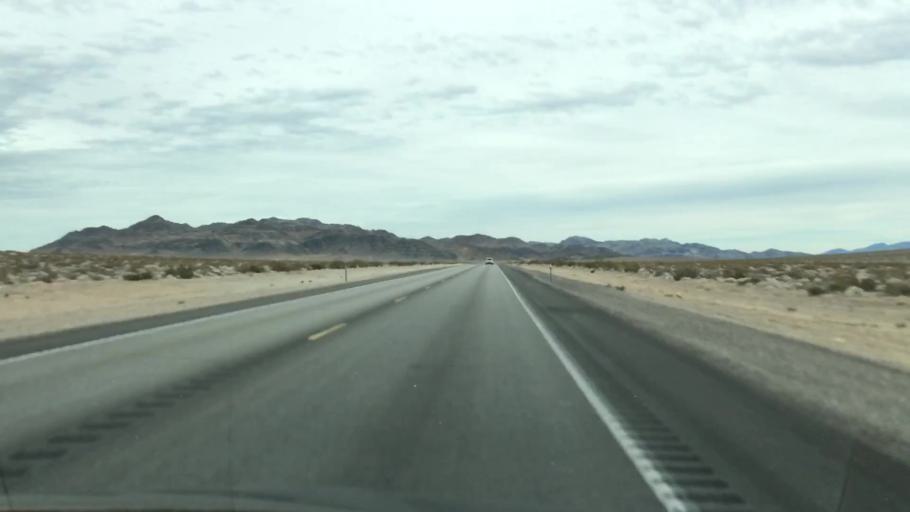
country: US
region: Nevada
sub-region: Nye County
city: Beatty
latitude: 36.6316
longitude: -116.3401
